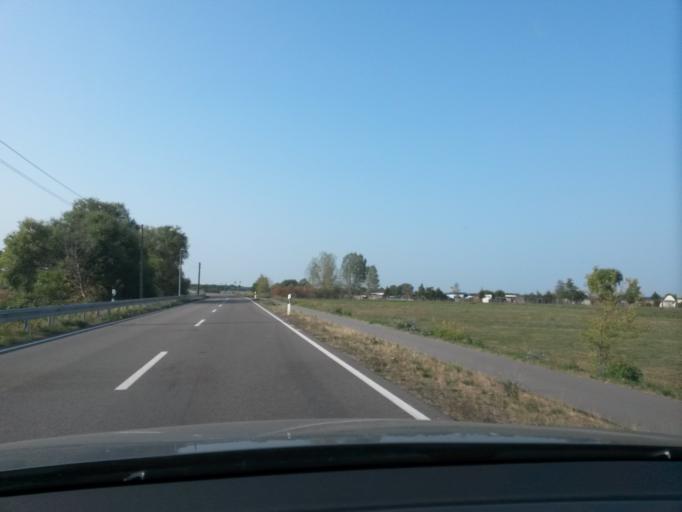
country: DE
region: Saxony-Anhalt
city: Tangermunde
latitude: 52.5322
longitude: 11.9459
